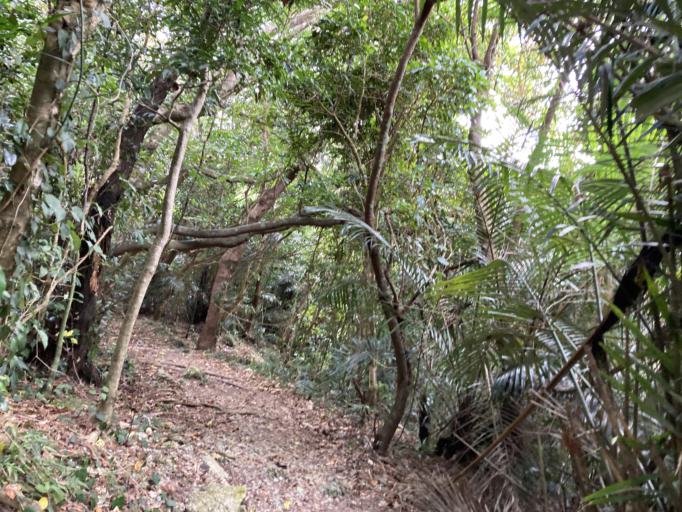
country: JP
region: Okinawa
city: Tomigusuku
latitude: 26.1428
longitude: 127.7822
